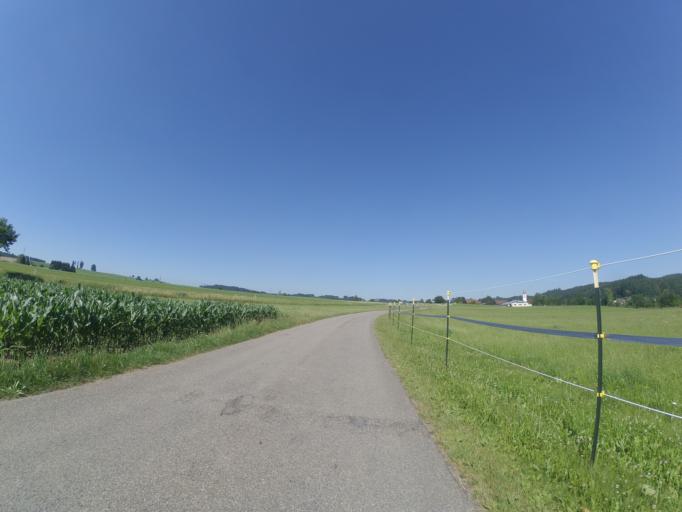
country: DE
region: Baden-Wuerttemberg
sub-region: Tuebingen Region
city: Leutkirch im Allgau
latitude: 47.8440
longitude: 9.9786
